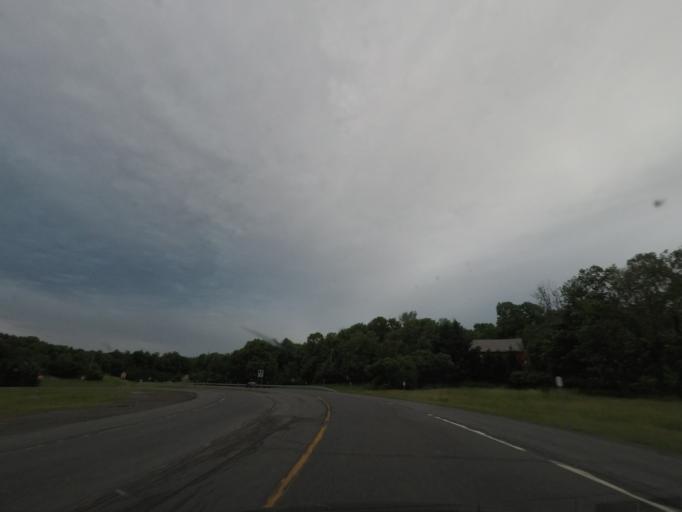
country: US
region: New York
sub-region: Columbia County
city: Chatham
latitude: 42.4226
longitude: -73.5477
